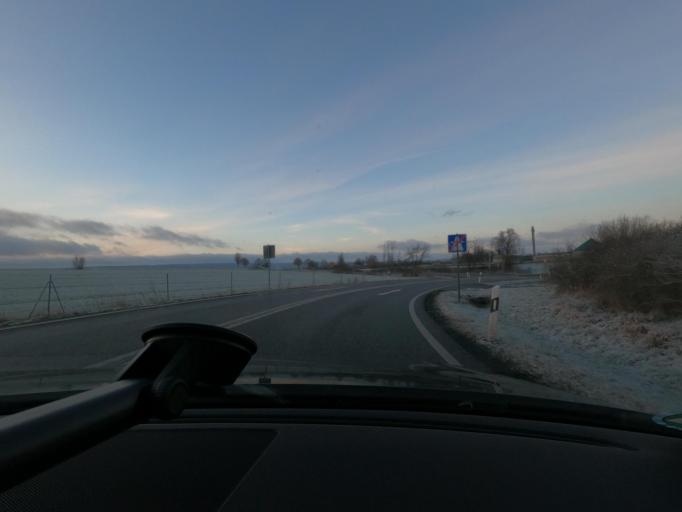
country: DE
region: Thuringia
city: Breitenworbis
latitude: 51.4018
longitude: 10.4355
